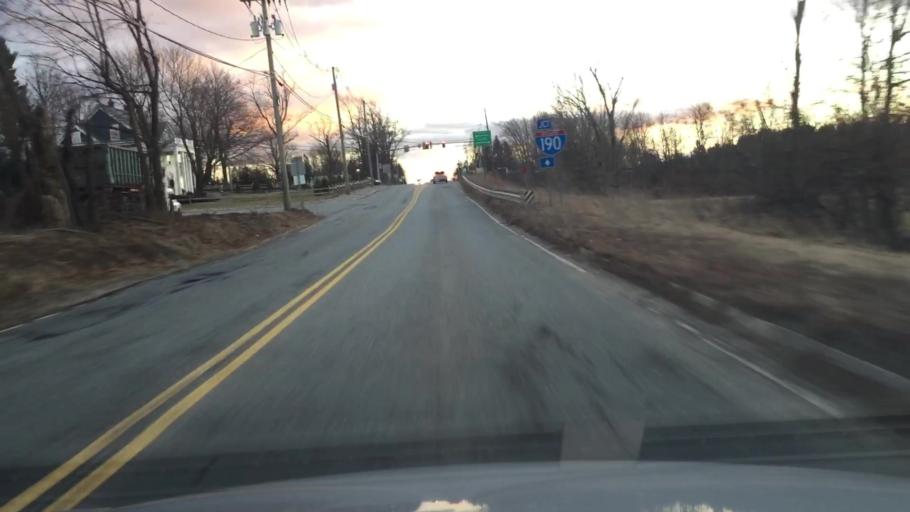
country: US
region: Massachusetts
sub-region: Worcester County
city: West Boylston
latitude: 42.4084
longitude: -71.7996
